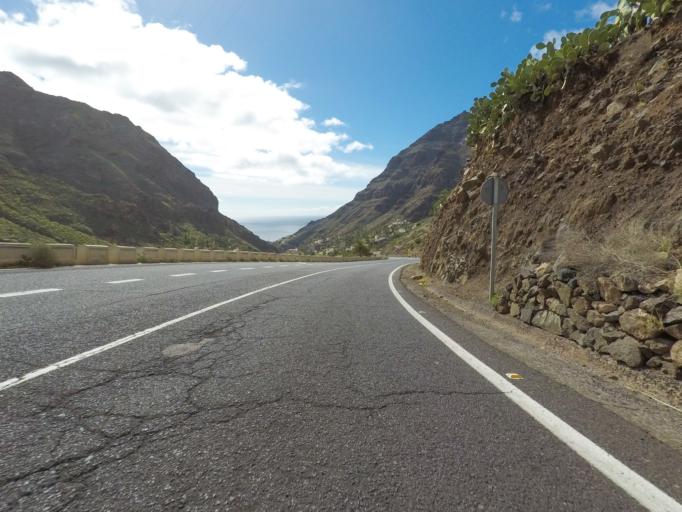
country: ES
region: Canary Islands
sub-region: Provincia de Santa Cruz de Tenerife
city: Vallehermosa
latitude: 28.1103
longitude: -17.3207
